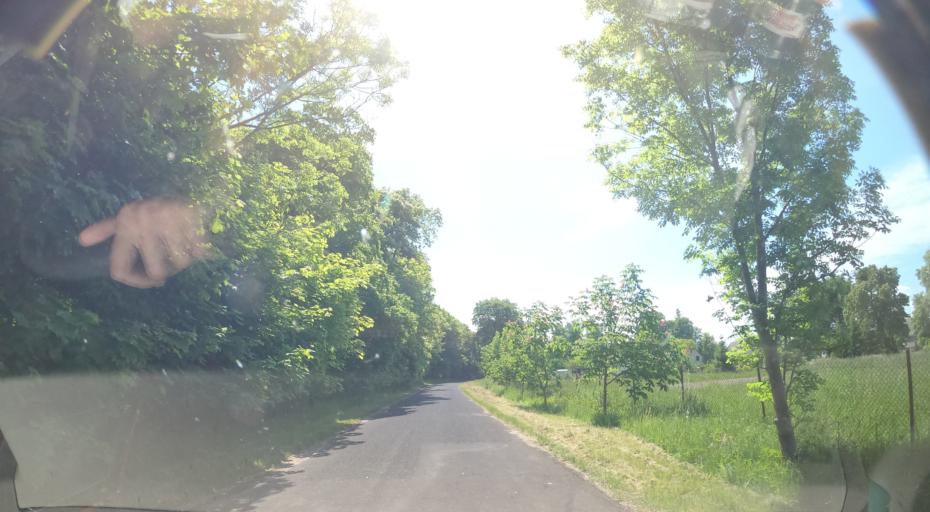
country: PL
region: West Pomeranian Voivodeship
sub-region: Powiat kolobrzeski
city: Ustronie Morskie
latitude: 54.1640
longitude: 15.8086
